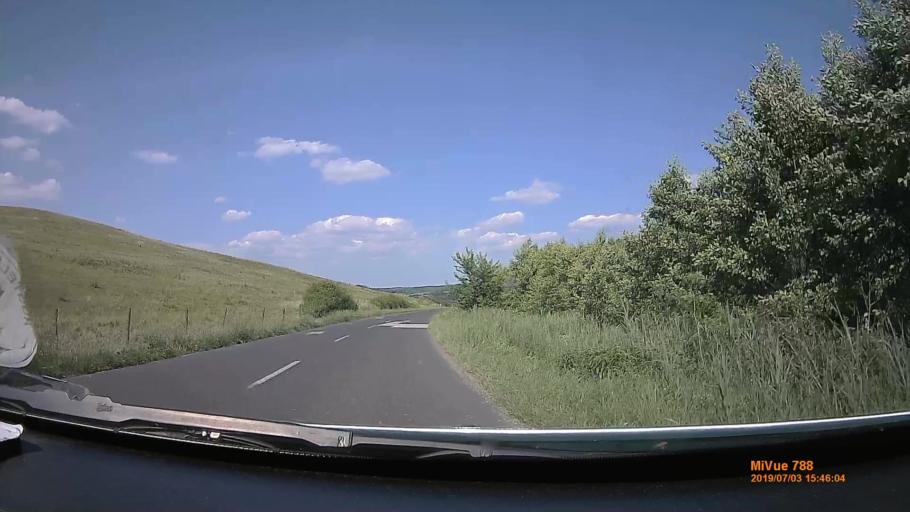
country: HU
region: Heves
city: Szilvasvarad
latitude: 48.1810
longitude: 20.4660
